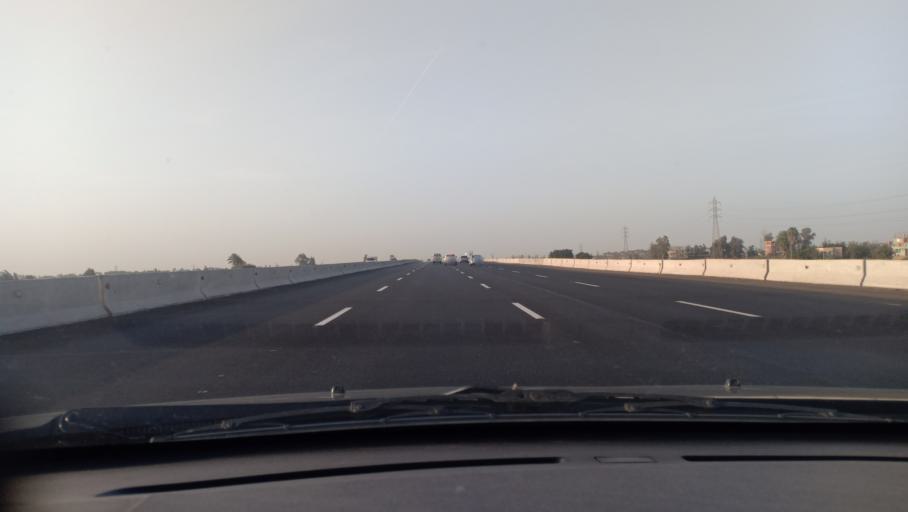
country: EG
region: Muhafazat al Qalyubiyah
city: Toukh
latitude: 30.2937
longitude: 31.2181
